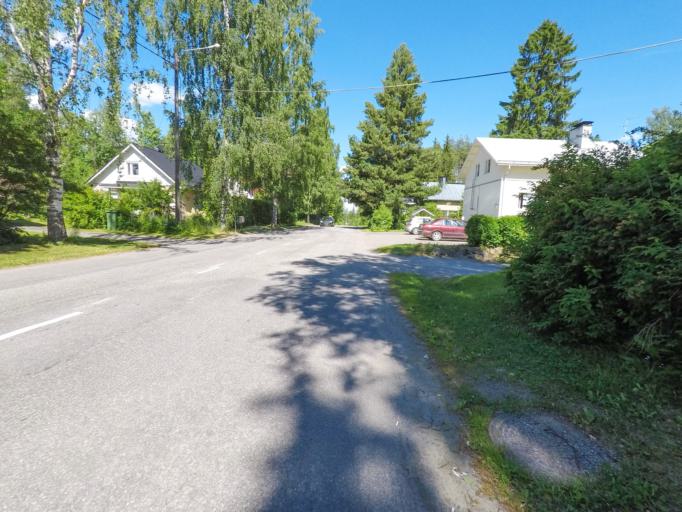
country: FI
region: Southern Savonia
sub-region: Savonlinna
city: Savonlinna
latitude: 61.8771
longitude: 28.8554
